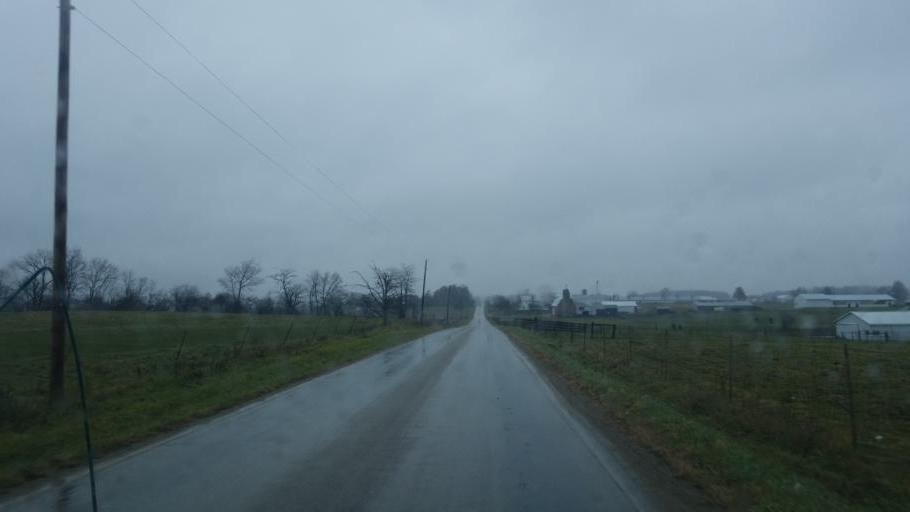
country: US
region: Indiana
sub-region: Adams County
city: Geneva
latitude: 40.6205
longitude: -84.9356
